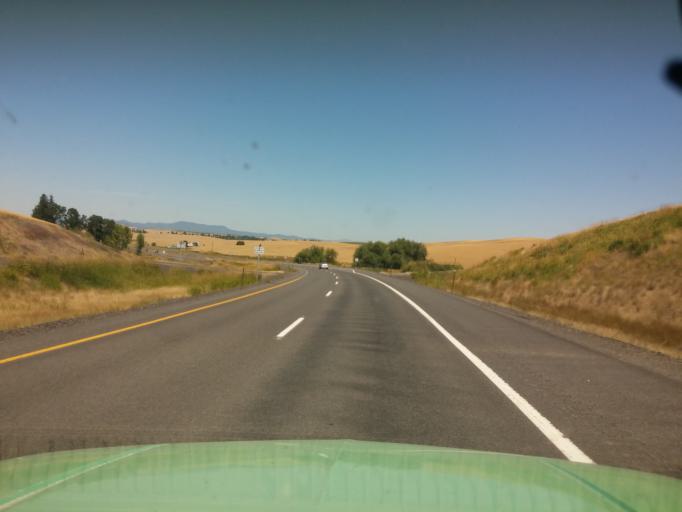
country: US
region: Idaho
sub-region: Nez Perce County
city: Lewiston
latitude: 46.5150
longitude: -116.9504
